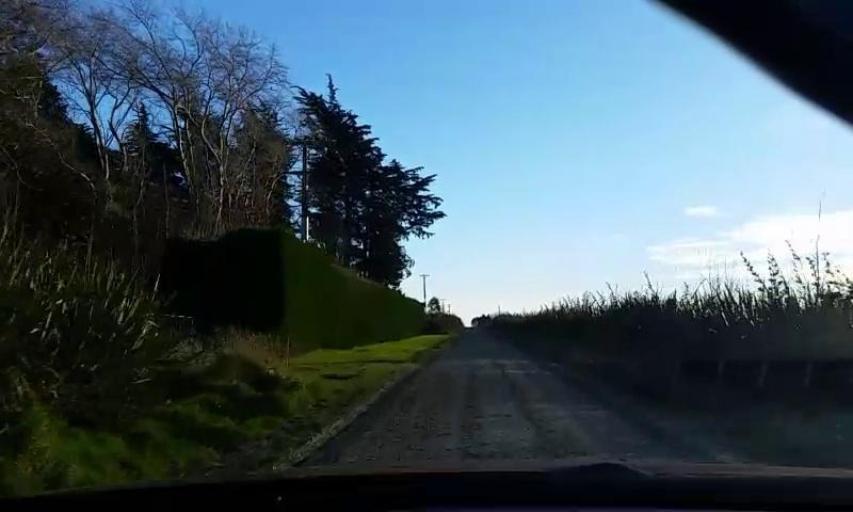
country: NZ
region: Southland
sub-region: Invercargill City
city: Invercargill
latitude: -46.2850
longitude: 168.5083
